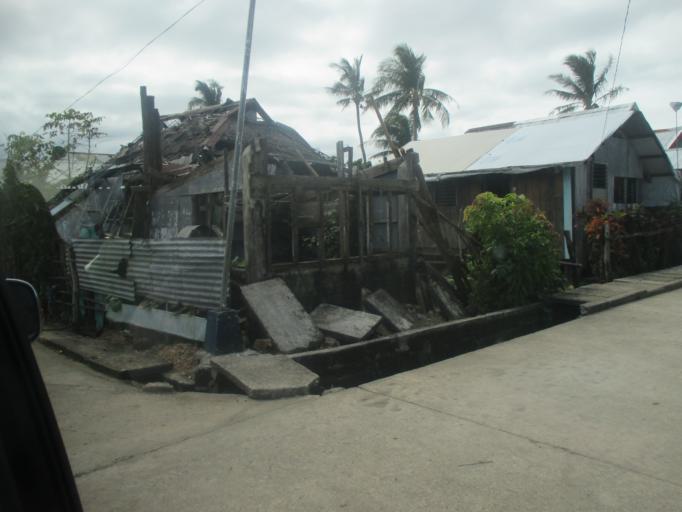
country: PH
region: Eastern Visayas
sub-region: Province of Eastern Samar
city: Salcedo
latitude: 11.1486
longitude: 125.6634
